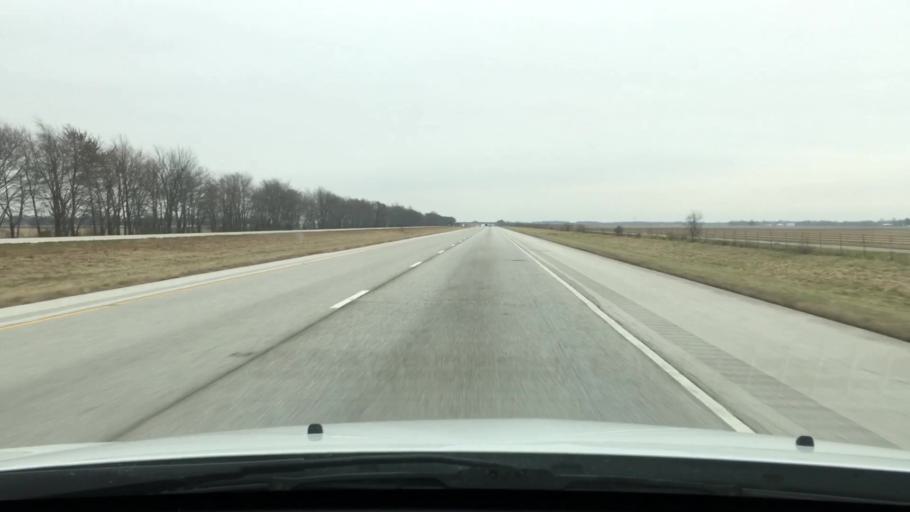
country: US
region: Illinois
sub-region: Scott County
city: Winchester
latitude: 39.6801
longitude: -90.3661
